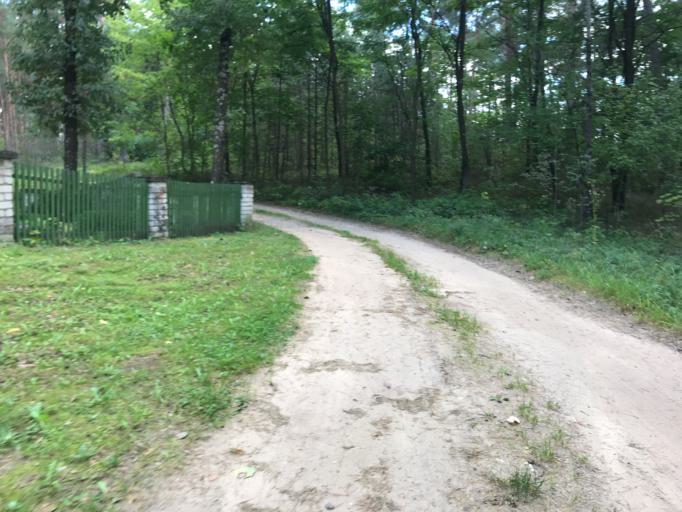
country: LT
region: Alytaus apskritis
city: Druskininkai
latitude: 54.0124
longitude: 23.9710
